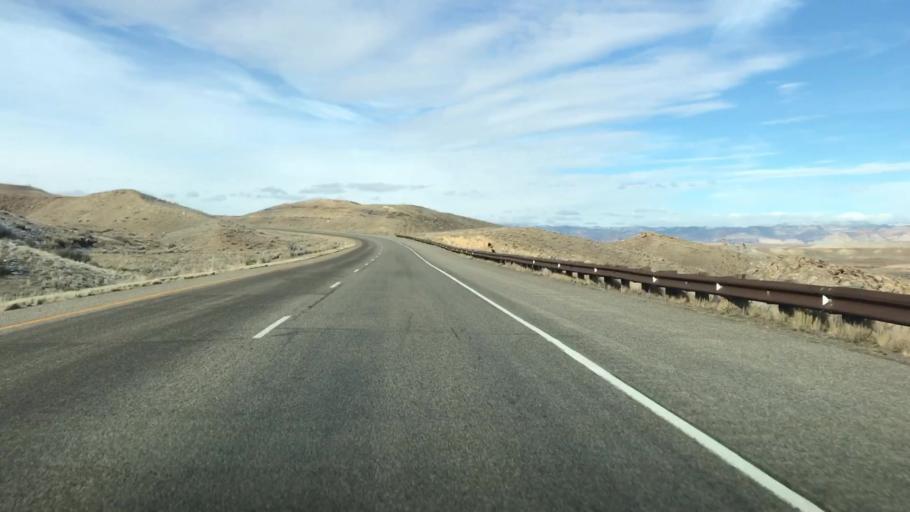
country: US
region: Colorado
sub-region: Mesa County
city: Loma
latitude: 39.2299
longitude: -108.9013
